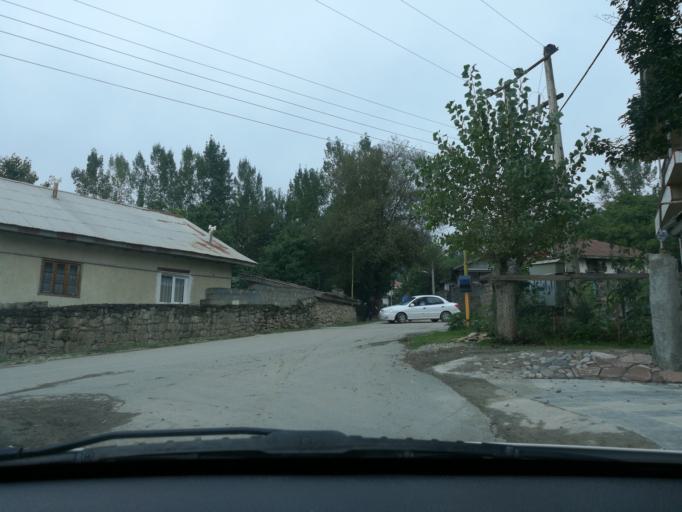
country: IR
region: Mazandaran
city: `Abbasabad
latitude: 36.4977
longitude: 51.2101
